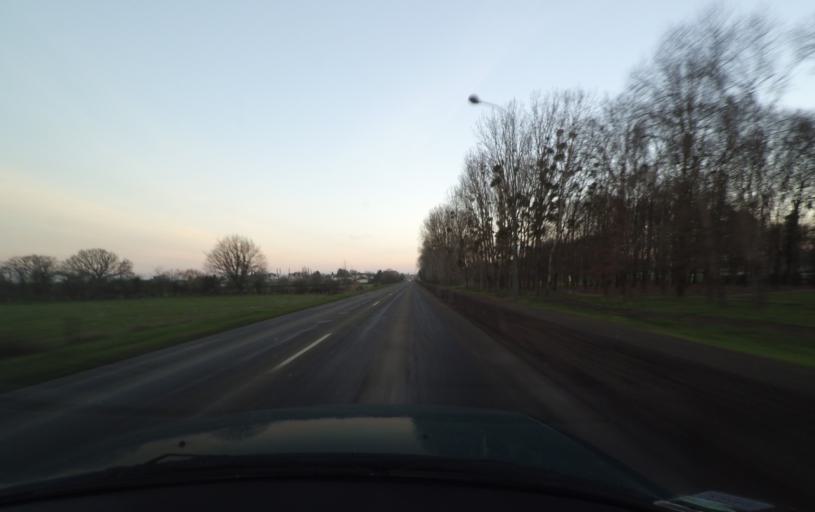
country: FR
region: Pays de la Loire
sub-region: Departement de la Mayenne
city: Evron
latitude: 48.1512
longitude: -0.4132
